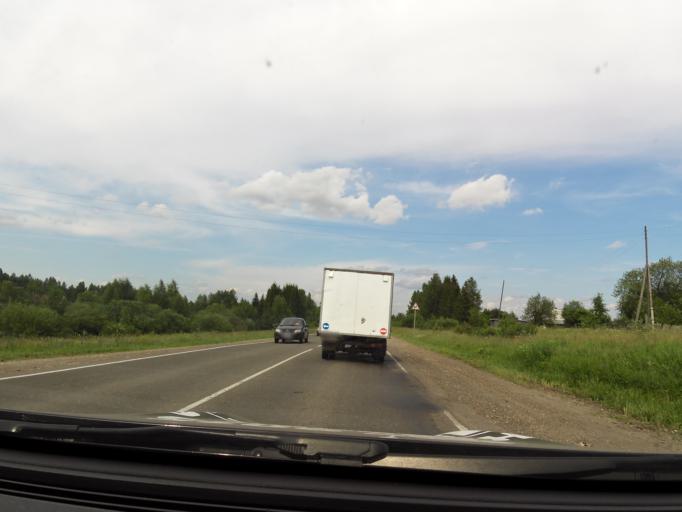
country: RU
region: Kirov
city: Stulovo
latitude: 58.7038
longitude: 50.0941
